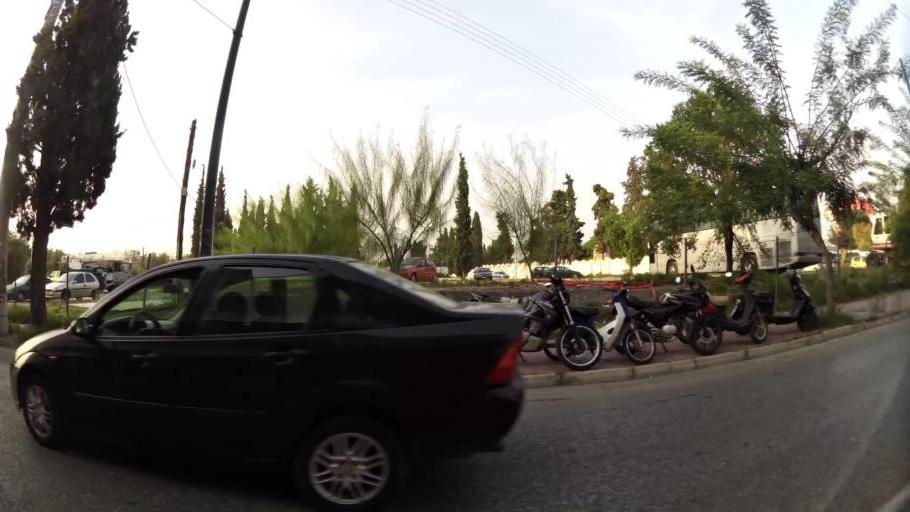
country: GR
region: Attica
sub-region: Nomarchia Athinas
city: Peristeri
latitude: 38.0206
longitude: 23.6866
